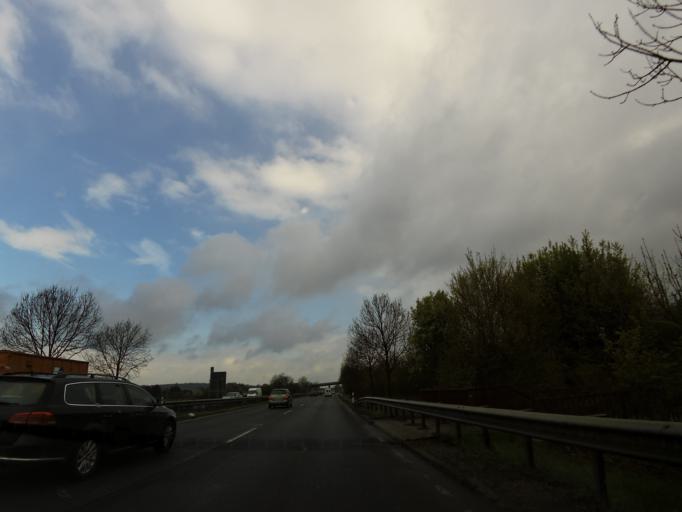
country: DE
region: Lower Saxony
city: Goettingen
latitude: 51.5624
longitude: 9.9200
